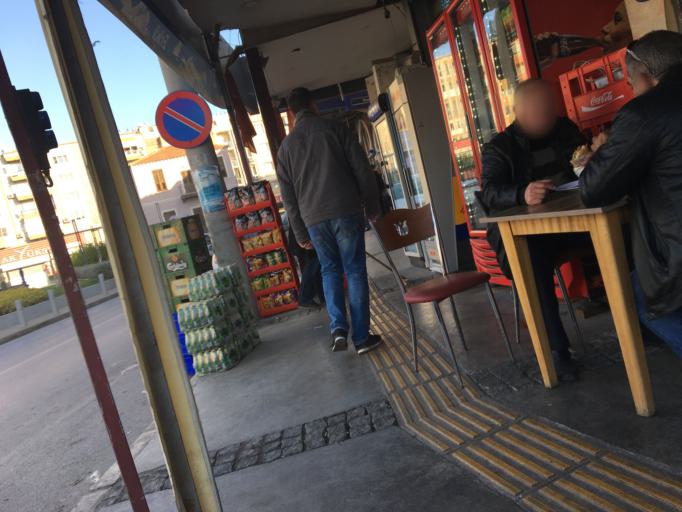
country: TR
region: Izmir
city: Buca
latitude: 38.3880
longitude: 27.1743
